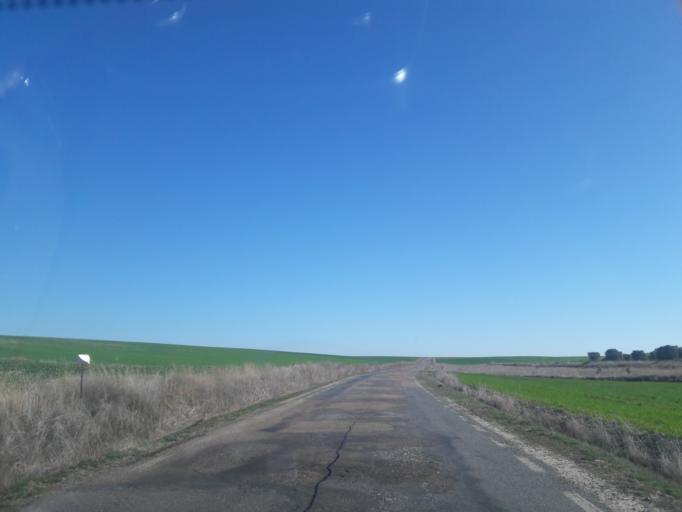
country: ES
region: Castille and Leon
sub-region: Provincia de Salamanca
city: Tordillos
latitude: 40.8647
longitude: -5.3376
